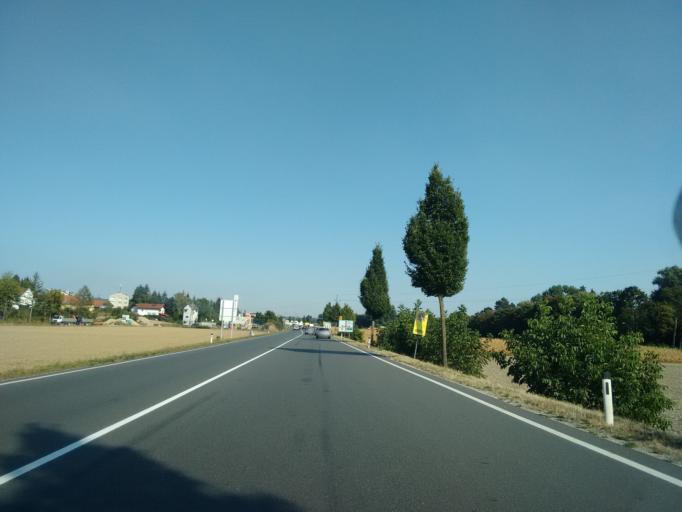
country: AT
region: Upper Austria
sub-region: Wels-Land
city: Marchtrenk
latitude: 48.1892
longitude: 14.1070
